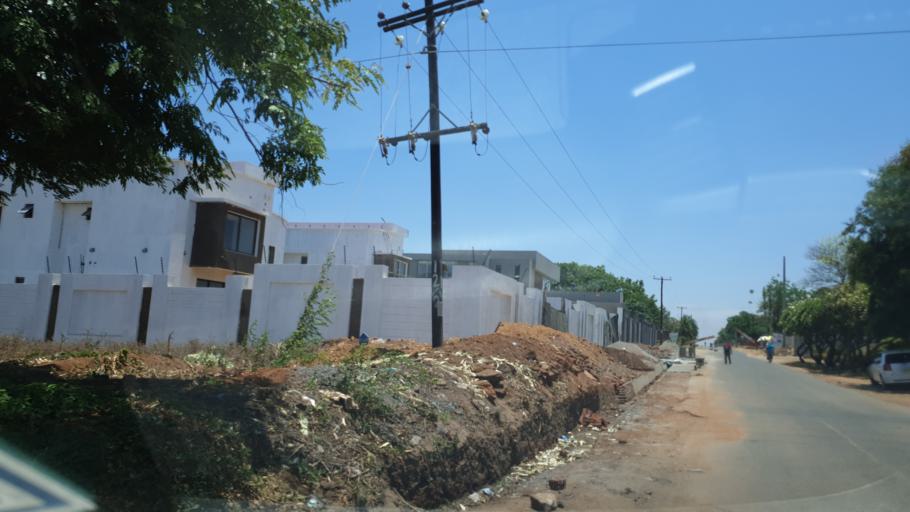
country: MW
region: Central Region
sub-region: Lilongwe District
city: Lilongwe
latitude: -13.9747
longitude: 33.7456
